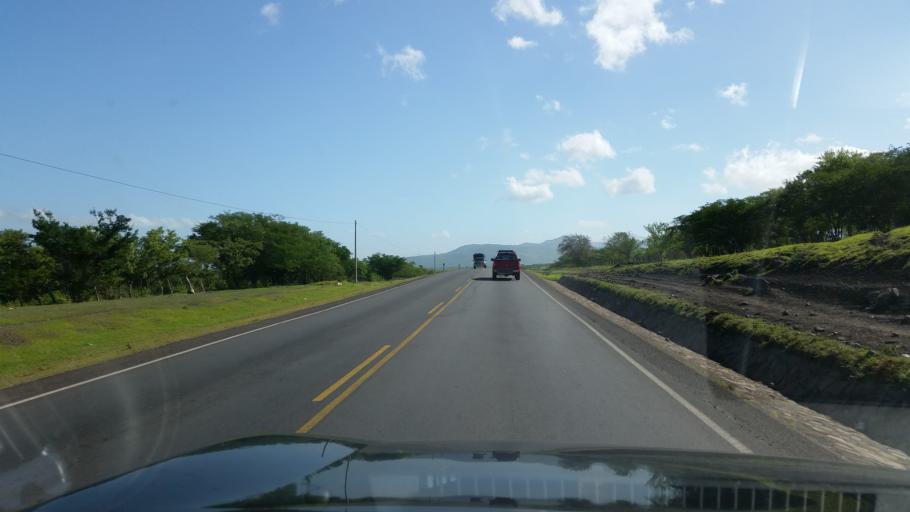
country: NI
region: Matagalpa
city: Ciudad Dario
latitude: 12.6793
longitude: -86.0871
